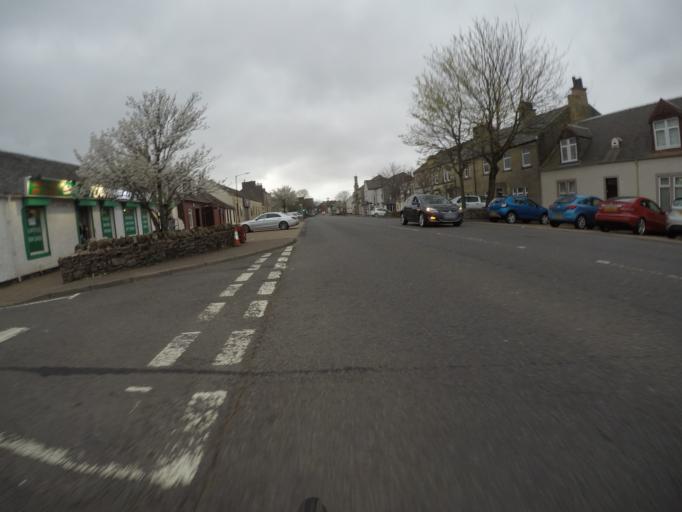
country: GB
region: Scotland
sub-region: North Ayrshire
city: Irvine
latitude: 55.6135
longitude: -4.6614
